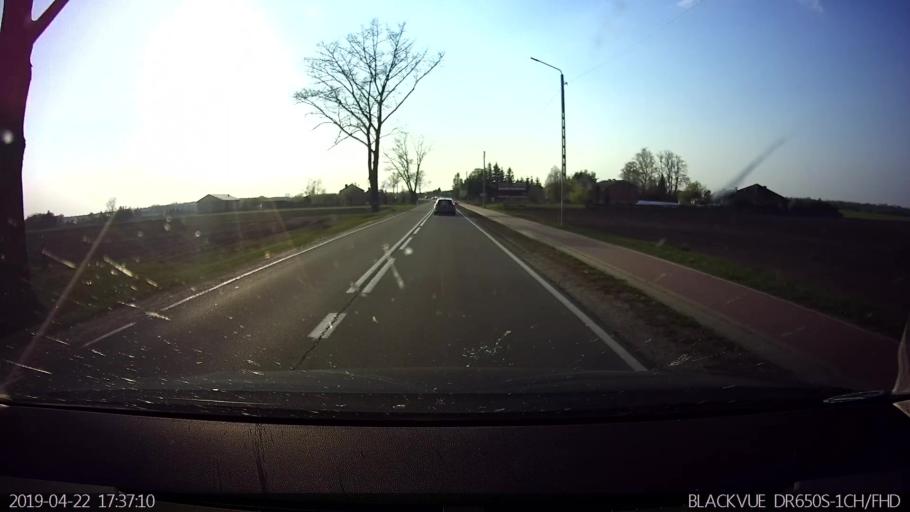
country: PL
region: Masovian Voivodeship
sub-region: Powiat sokolowski
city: Sokolow Podlaski
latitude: 52.4085
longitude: 22.1782
